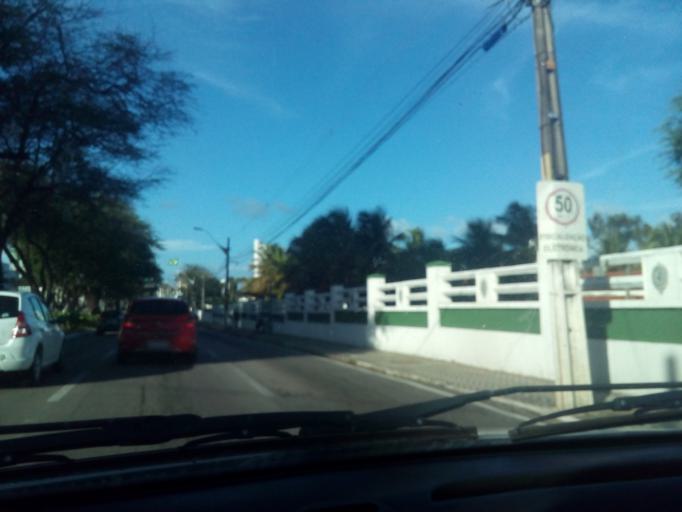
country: BR
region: Rio Grande do Norte
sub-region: Natal
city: Natal
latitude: -5.8043
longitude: -35.2019
